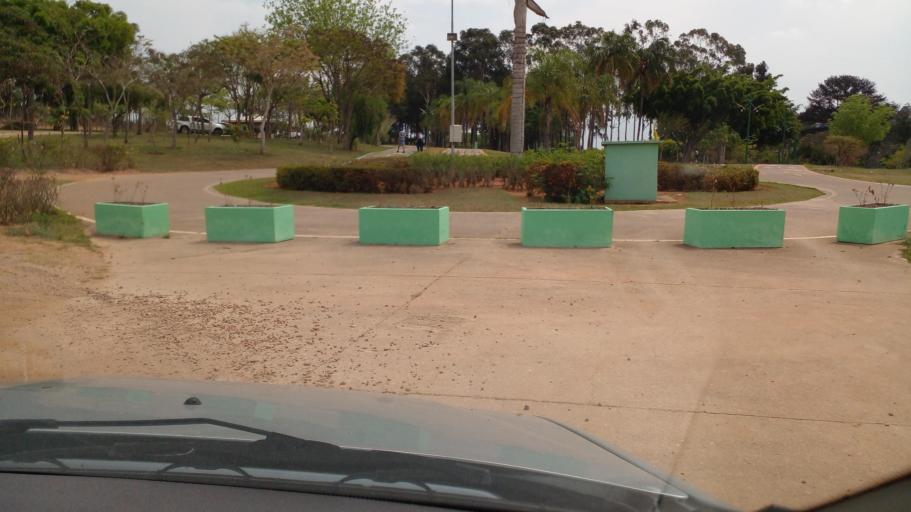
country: BR
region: Sao Paulo
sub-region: Jundiai
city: Jundiai
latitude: -23.1506
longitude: -46.8807
